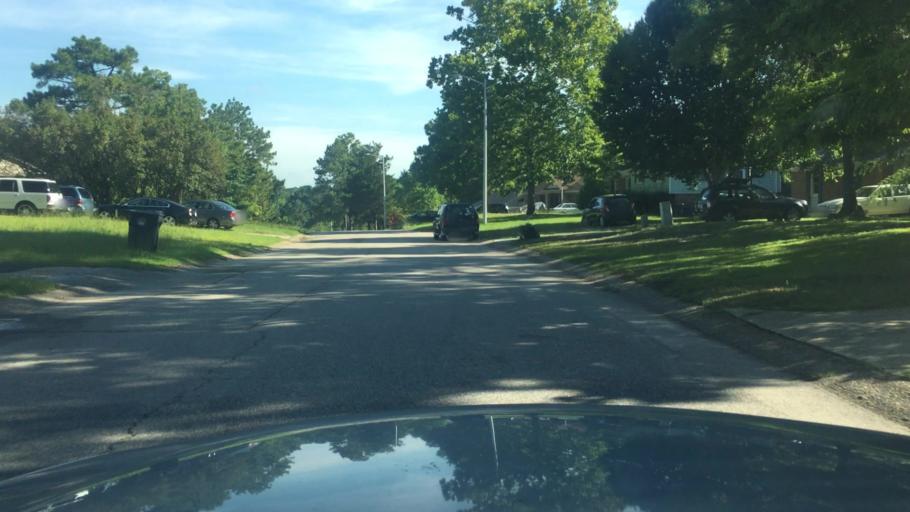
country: US
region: North Carolina
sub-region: Cumberland County
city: Fayetteville
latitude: 35.1375
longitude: -78.8921
